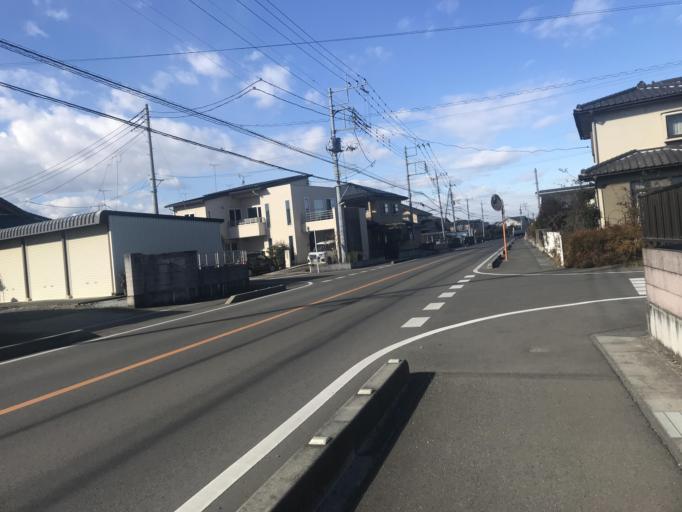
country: JP
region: Tochigi
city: Kaminokawa
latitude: 36.3775
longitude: 139.8779
